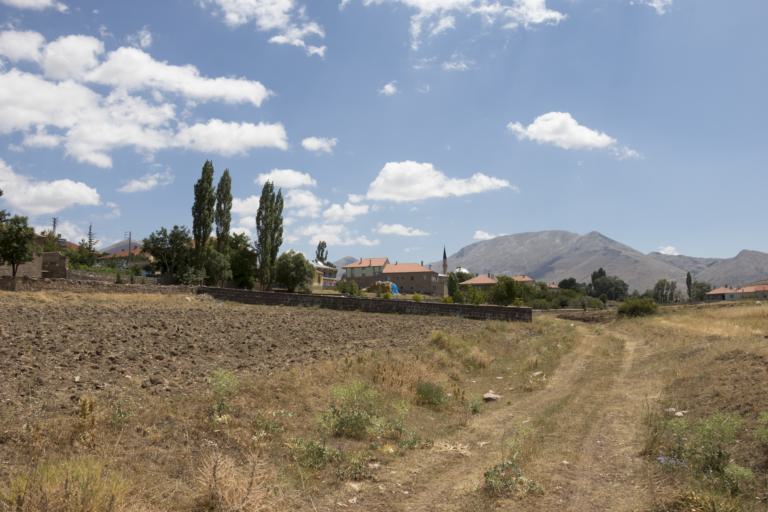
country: TR
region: Kayseri
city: Toklar
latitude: 38.4063
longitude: 36.0774
